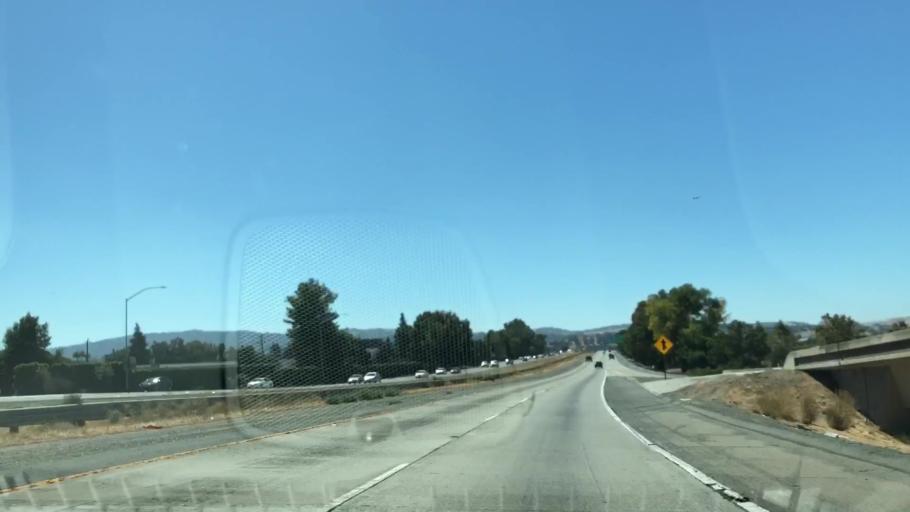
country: US
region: California
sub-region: Contra Costa County
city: Concord
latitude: 38.0044
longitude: -122.0400
